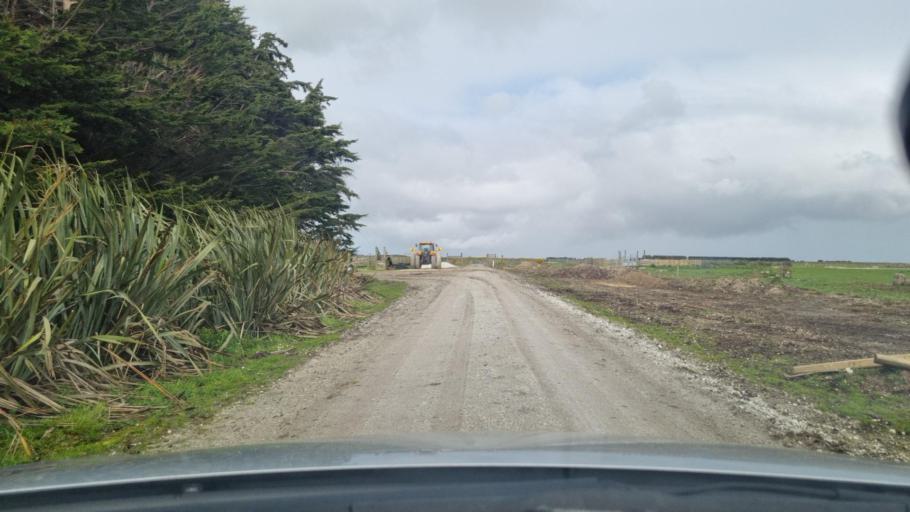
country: NZ
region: Southland
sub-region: Invercargill City
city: Bluff
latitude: -46.5174
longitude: 168.3624
